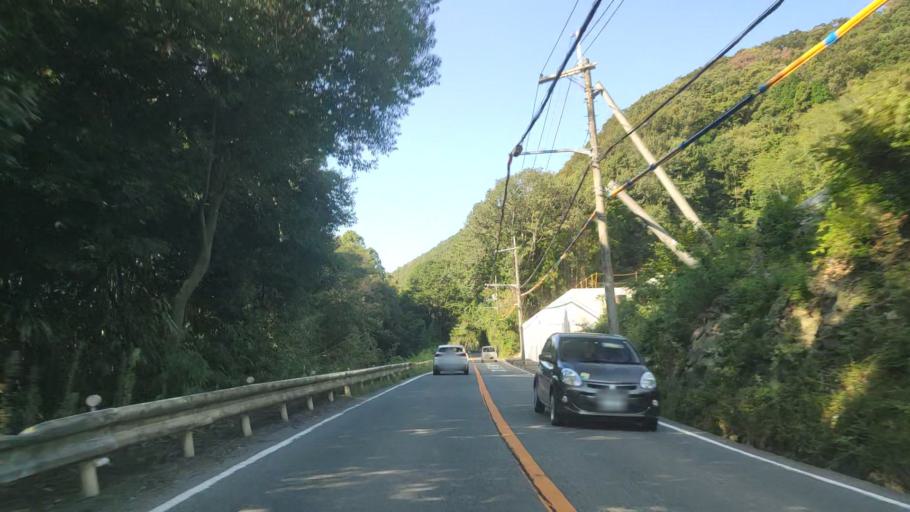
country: JP
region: Hyogo
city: Sandacho
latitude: 34.7940
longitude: 135.2150
